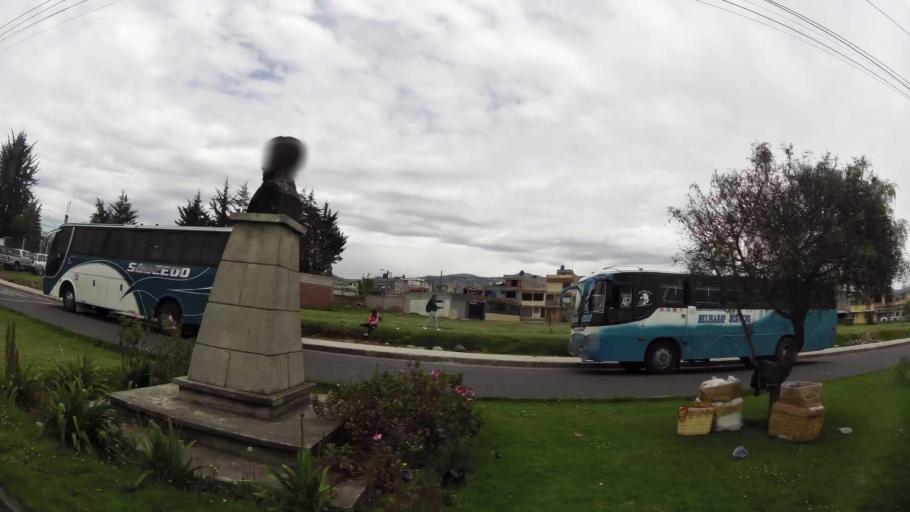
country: EC
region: Cotopaxi
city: San Miguel de Salcedo
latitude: -1.0315
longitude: -78.5904
